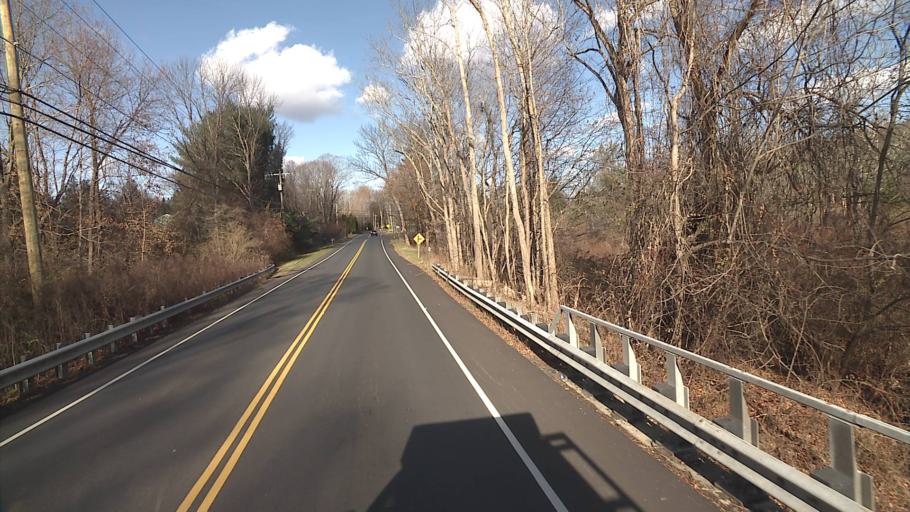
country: US
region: Connecticut
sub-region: Fairfield County
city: Bethel
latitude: 41.3224
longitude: -73.4240
